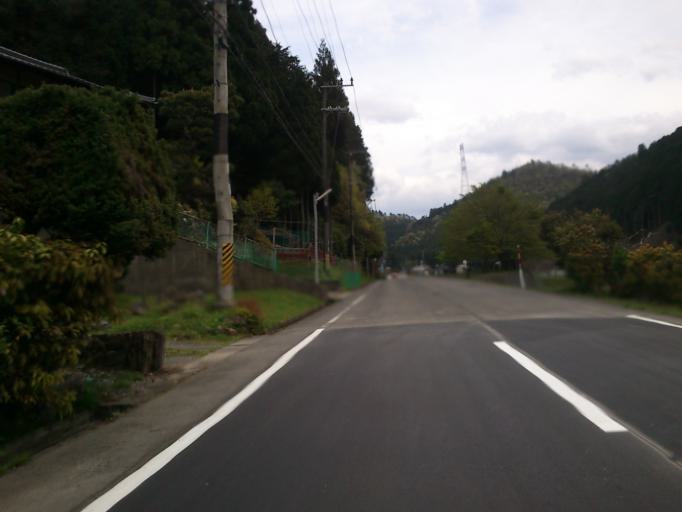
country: JP
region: Kyoto
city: Kameoka
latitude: 35.2057
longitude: 135.6092
